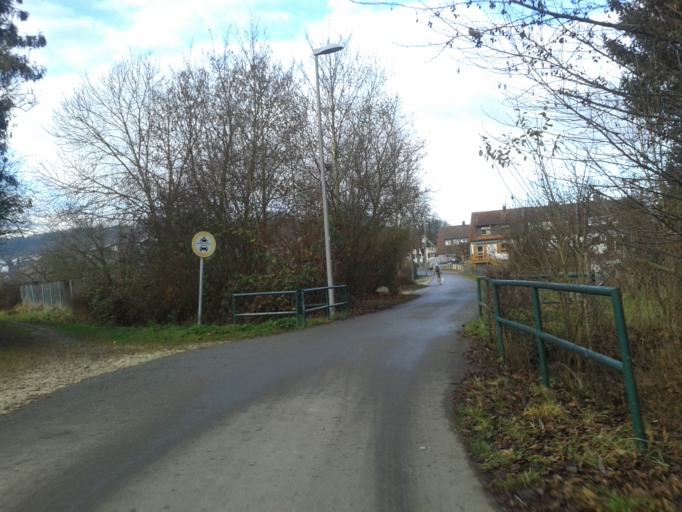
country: DE
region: Baden-Wuerttemberg
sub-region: Tuebingen Region
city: Ulm
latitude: 48.4005
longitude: 9.9420
